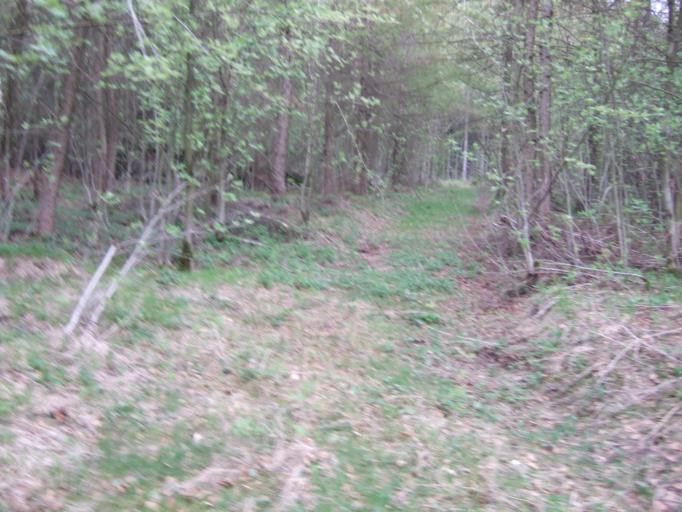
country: DE
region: Saxony
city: Rechenberg-Bienenmuhle
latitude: 50.7471
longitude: 13.5795
